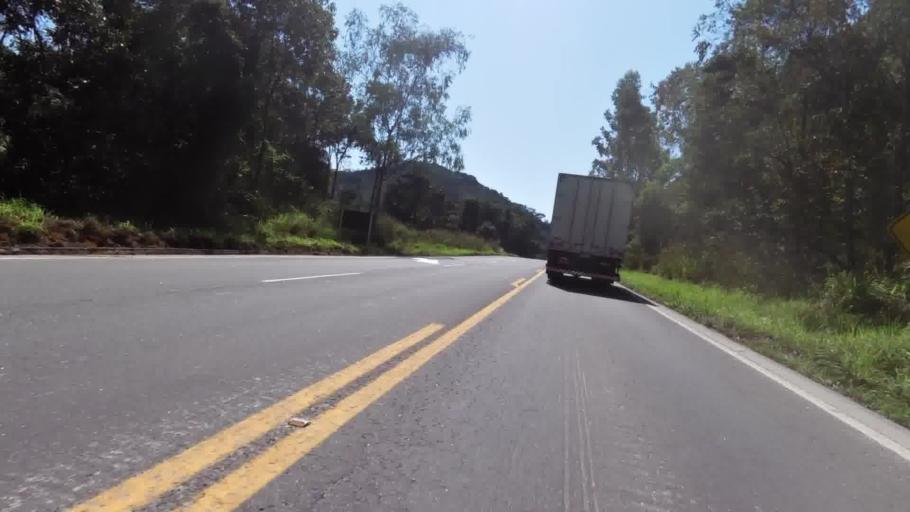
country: BR
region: Espirito Santo
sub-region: Marechal Floriano
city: Marechal Floriano
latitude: -20.4190
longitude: -40.8730
